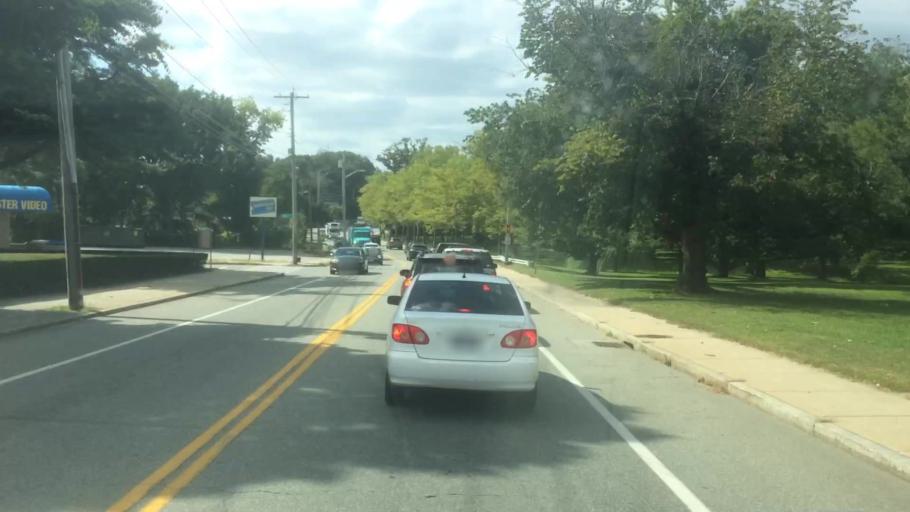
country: US
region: Rhode Island
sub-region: Providence County
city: Cranston
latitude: 41.7724
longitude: -71.4118
